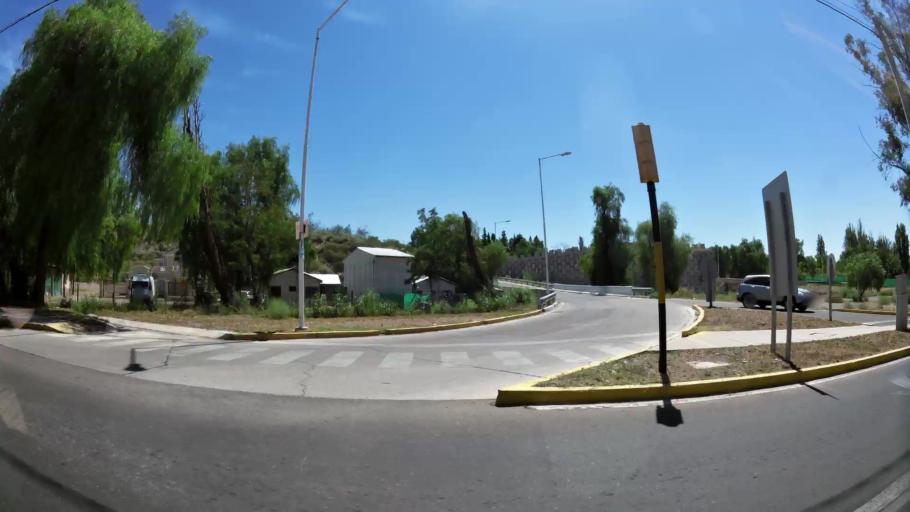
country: AR
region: Mendoza
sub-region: Departamento de Godoy Cruz
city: Godoy Cruz
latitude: -32.9605
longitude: -68.8652
